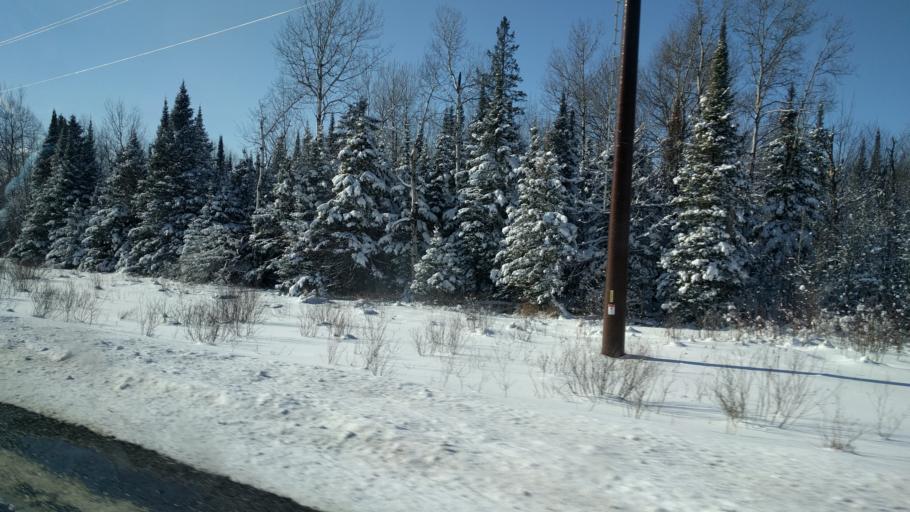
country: US
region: Wisconsin
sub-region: Iron County
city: Hurley
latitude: 46.3949
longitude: -90.3437
